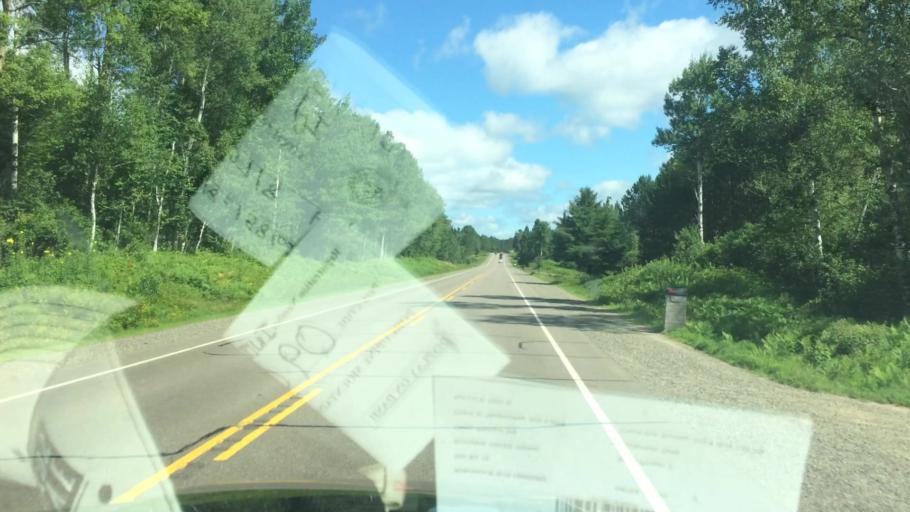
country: US
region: Wisconsin
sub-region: Oneida County
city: Rhinelander
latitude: 45.5821
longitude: -89.5694
